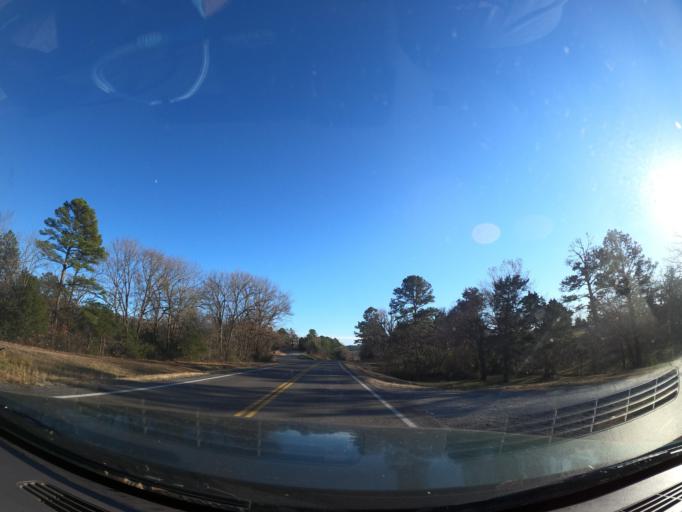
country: US
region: Oklahoma
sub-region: Latimer County
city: Wilburton
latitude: 34.9527
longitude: -95.3425
